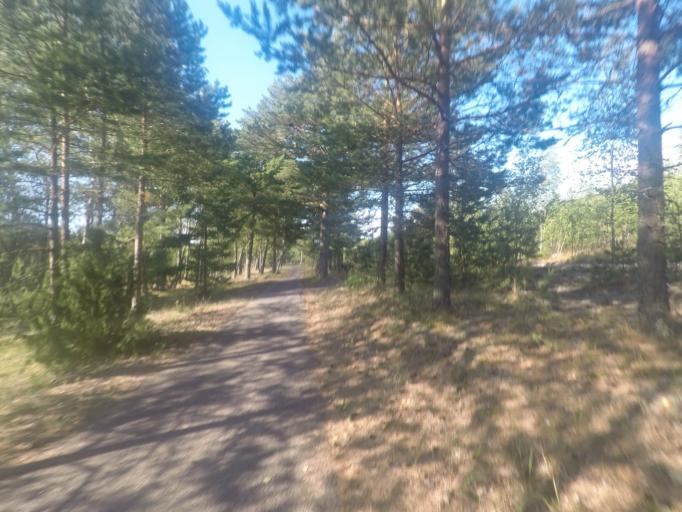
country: LT
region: Klaipedos apskritis
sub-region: Klaipeda
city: Klaipeda
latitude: 55.5691
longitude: 21.1129
